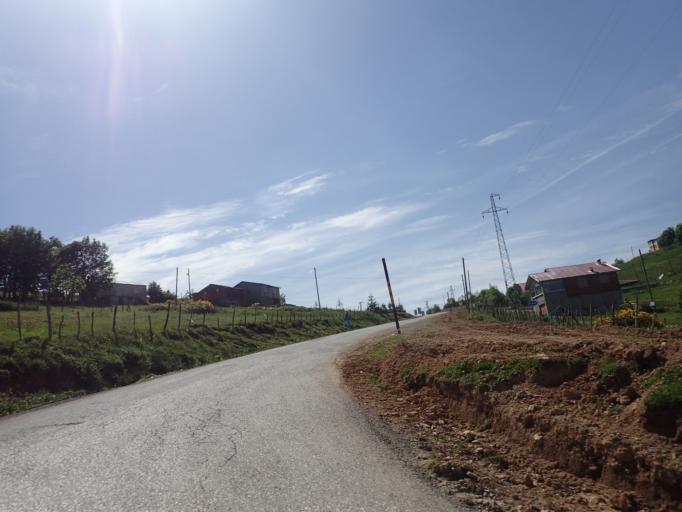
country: TR
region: Ordu
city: Yesilce
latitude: 40.6310
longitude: 37.9531
